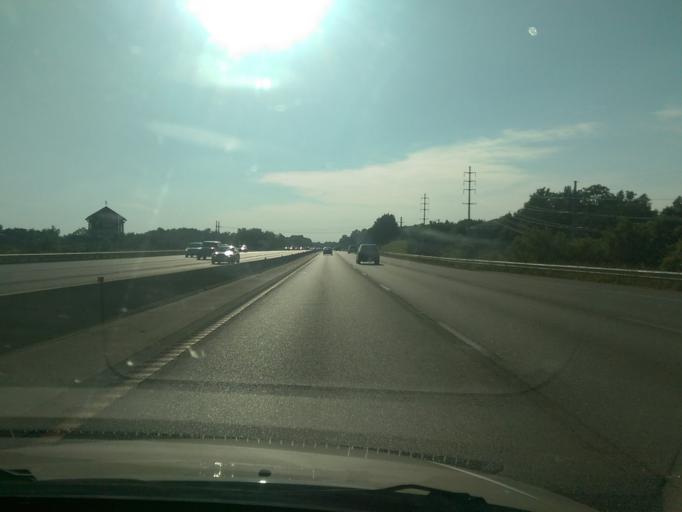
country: US
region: Missouri
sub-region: Jackson County
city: East Independence
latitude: 39.0428
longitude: -94.3689
